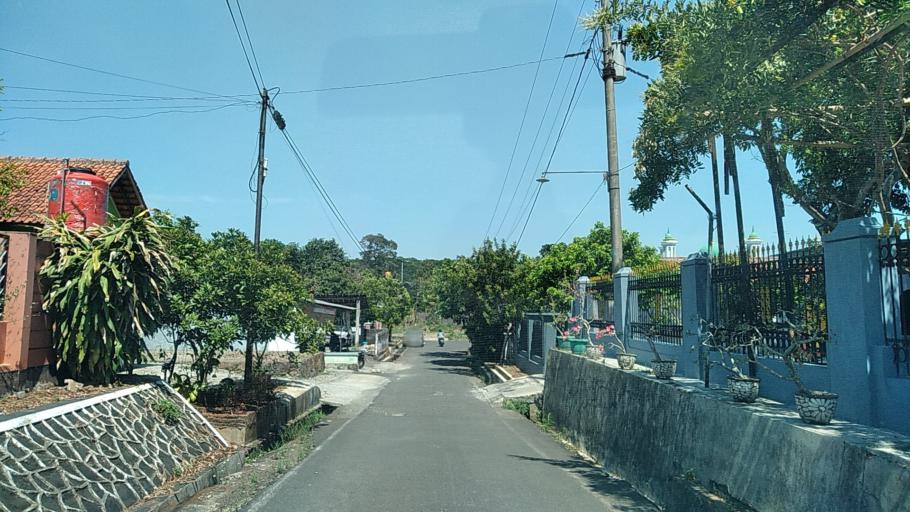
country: ID
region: Central Java
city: Ungaran
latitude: -7.0982
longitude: 110.4088
